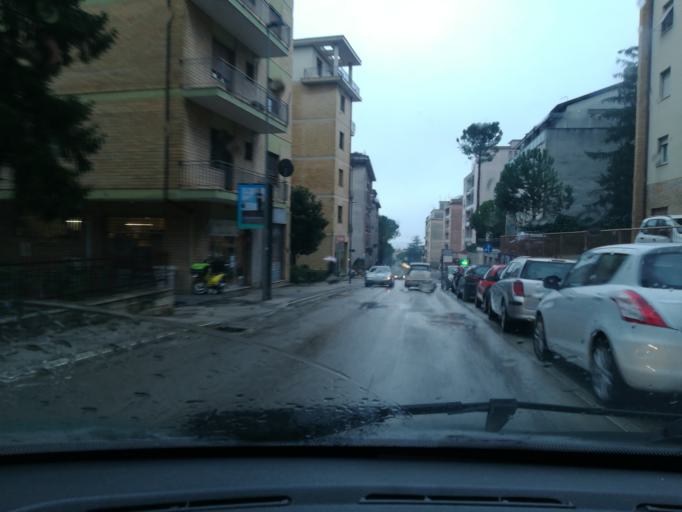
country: IT
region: The Marches
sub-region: Provincia di Macerata
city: Macerata
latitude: 43.2944
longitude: 13.4360
